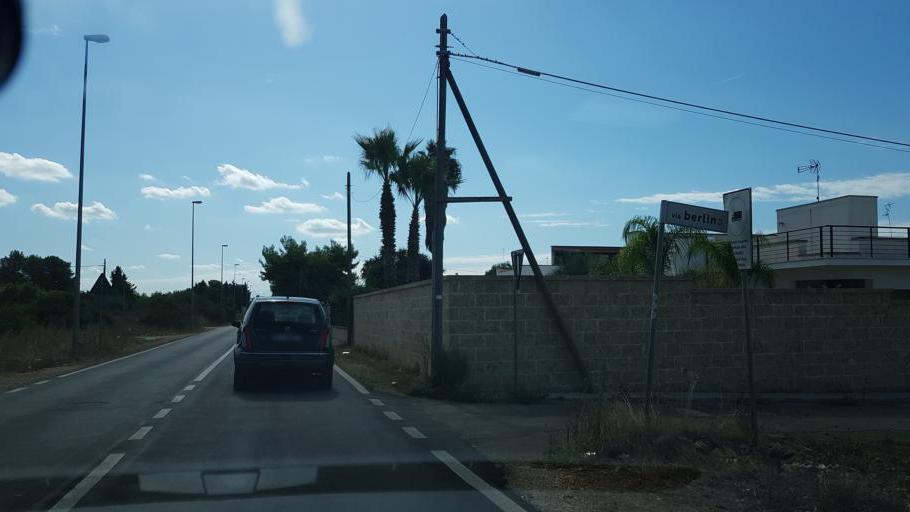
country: IT
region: Apulia
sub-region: Provincia di Lecce
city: Porto Cesareo
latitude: 40.2472
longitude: 17.9126
